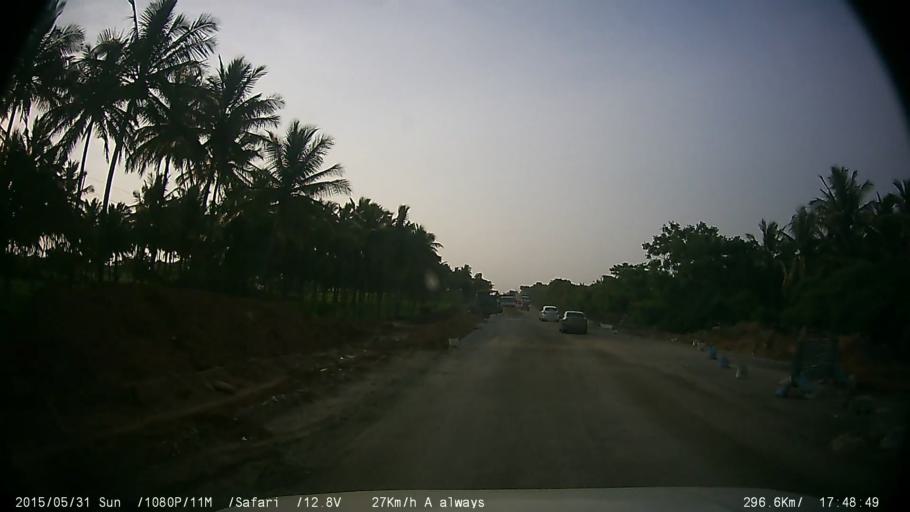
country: IN
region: Karnataka
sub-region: Mysore
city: Nanjangud
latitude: 11.9684
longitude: 76.6701
